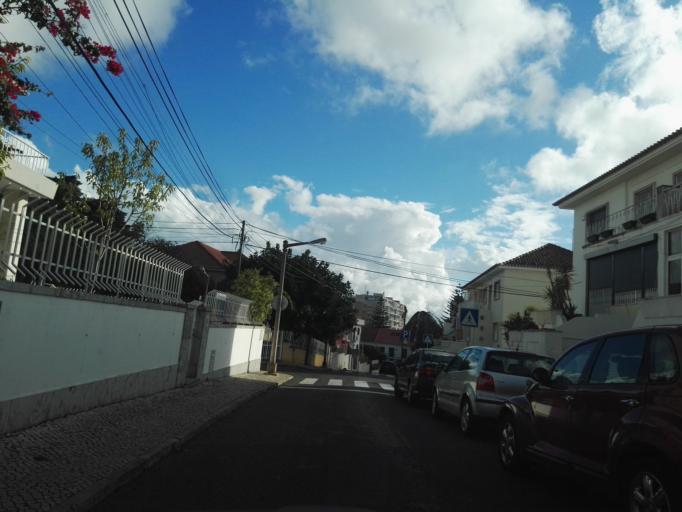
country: PT
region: Lisbon
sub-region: Lisbon
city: Lisbon
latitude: 38.7520
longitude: -9.1359
